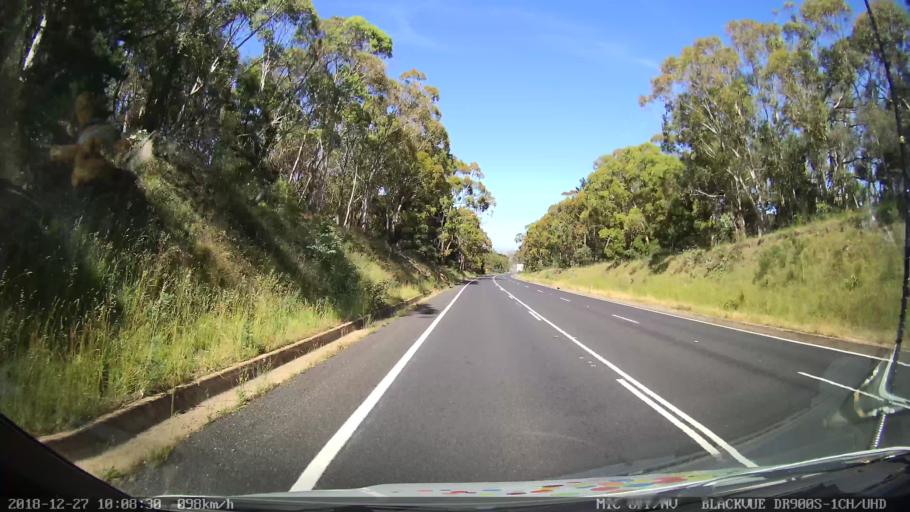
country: AU
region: New South Wales
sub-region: Lithgow
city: Portland
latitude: -33.4480
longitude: 149.8248
